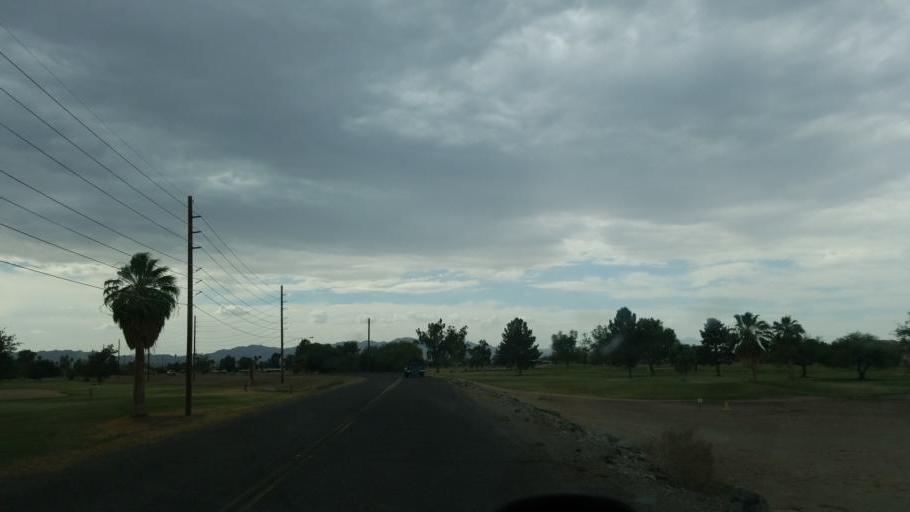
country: US
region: California
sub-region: San Bernardino County
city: Needles
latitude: 34.8424
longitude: -114.6003
